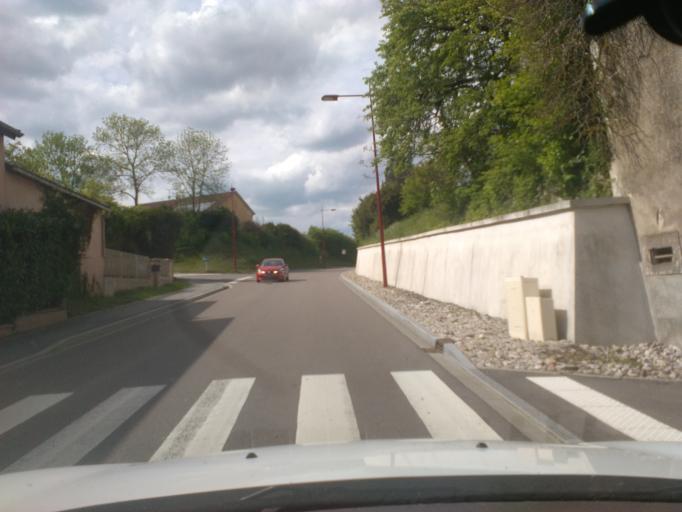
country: FR
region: Lorraine
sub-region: Departement des Vosges
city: Mirecourt
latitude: 48.2669
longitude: 6.1413
